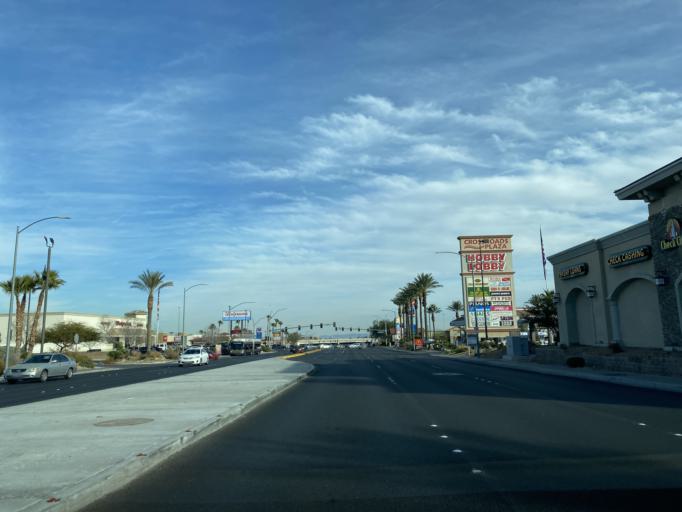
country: US
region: Nevada
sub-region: Clark County
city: Summerlin South
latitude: 36.1000
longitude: -115.2992
